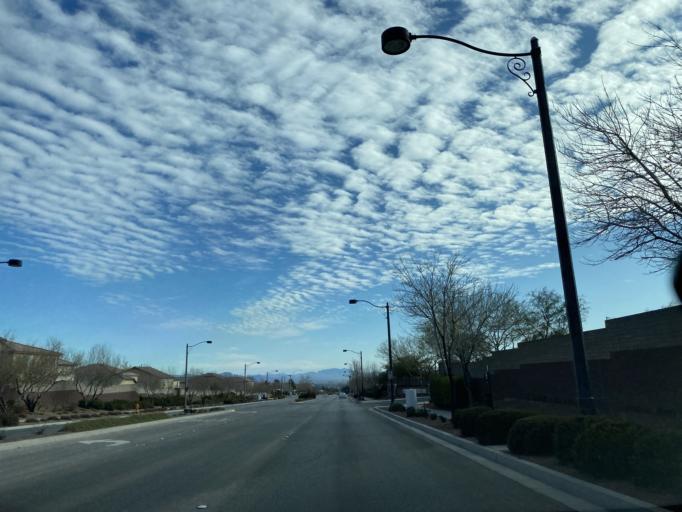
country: US
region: Nevada
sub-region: Clark County
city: Summerlin South
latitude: 36.2882
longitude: -115.3225
